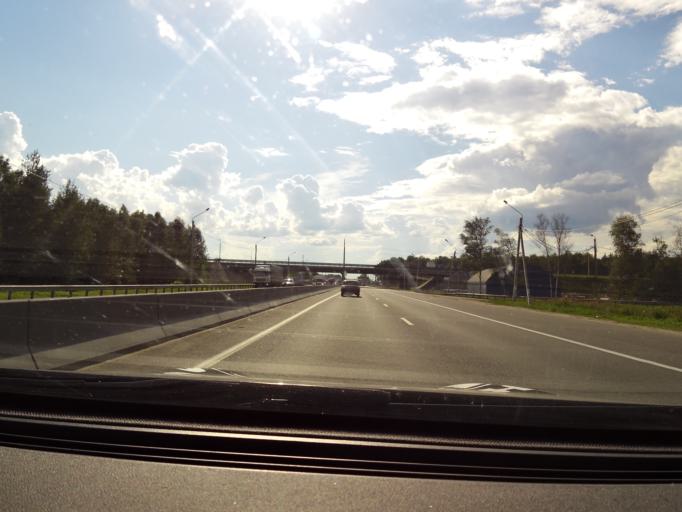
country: RU
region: Nizjnij Novgorod
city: Gorbatovka
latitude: 56.3068
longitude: 43.6878
